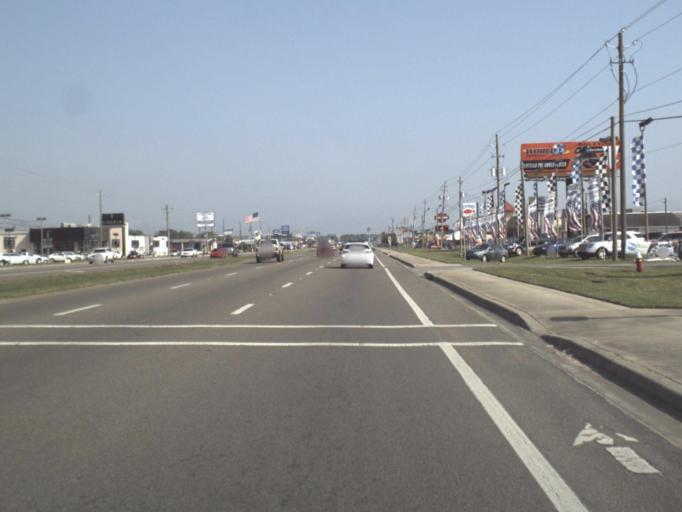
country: US
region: Florida
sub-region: Escambia County
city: Brent
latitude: 30.4813
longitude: -87.2551
